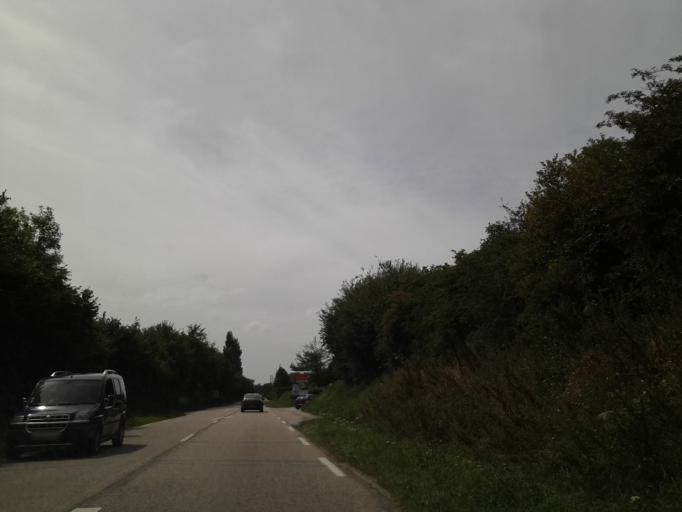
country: FR
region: Lower Normandy
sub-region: Departement de la Manche
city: Valognes
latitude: 49.5017
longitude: -1.4929
